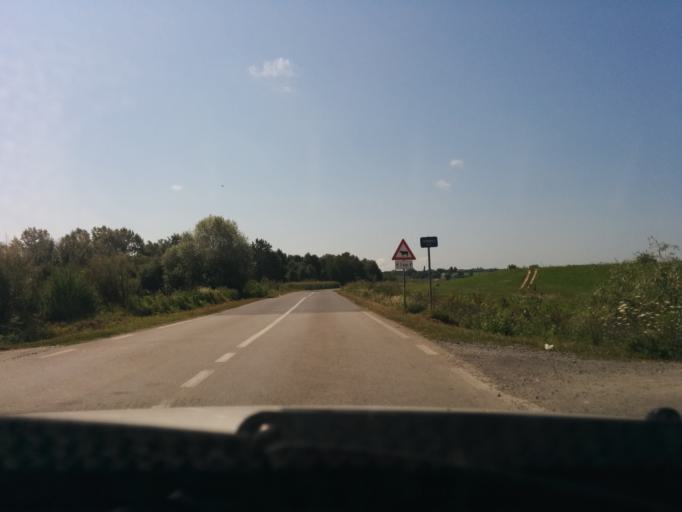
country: HR
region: Sisacko-Moslavacka
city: Lipovljani
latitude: 45.4396
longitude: 16.9039
